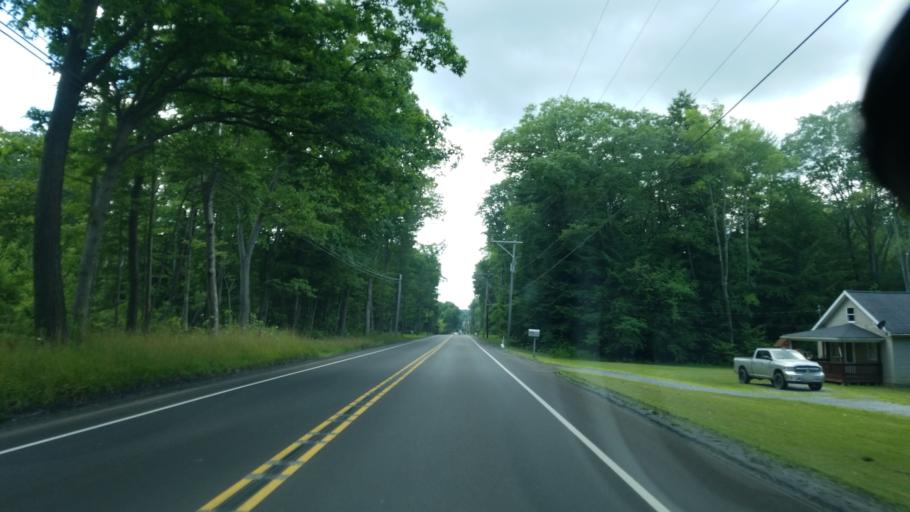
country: US
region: Pennsylvania
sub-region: Jefferson County
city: Brookville
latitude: 41.2574
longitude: -79.1078
